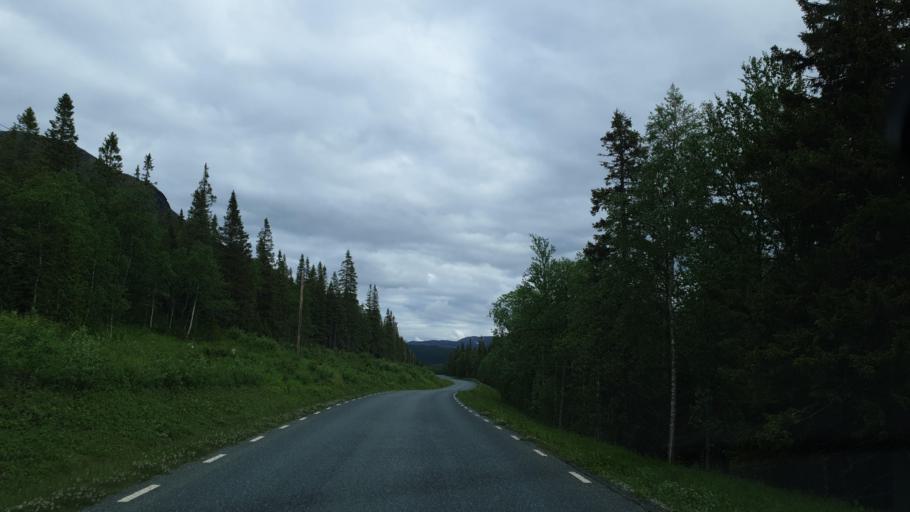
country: SE
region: Vaesterbotten
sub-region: Vilhelmina Kommun
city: Sjoberg
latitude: 65.2447
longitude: 15.4301
